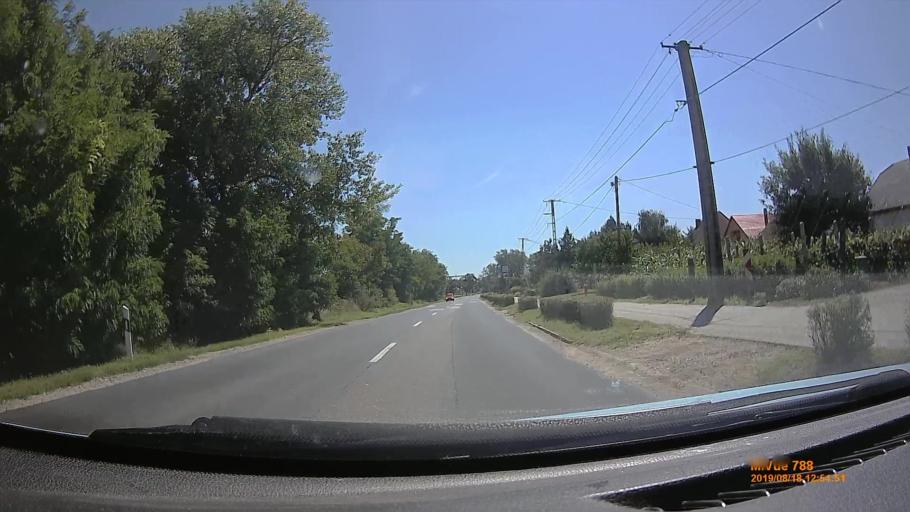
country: HU
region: Fejer
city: Aba
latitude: 47.0383
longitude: 18.5340
